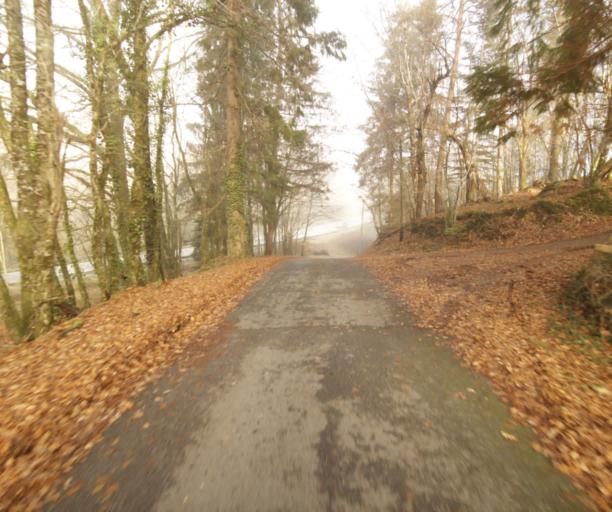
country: FR
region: Limousin
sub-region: Departement de la Correze
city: Laguenne
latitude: 45.2607
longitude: 1.7887
